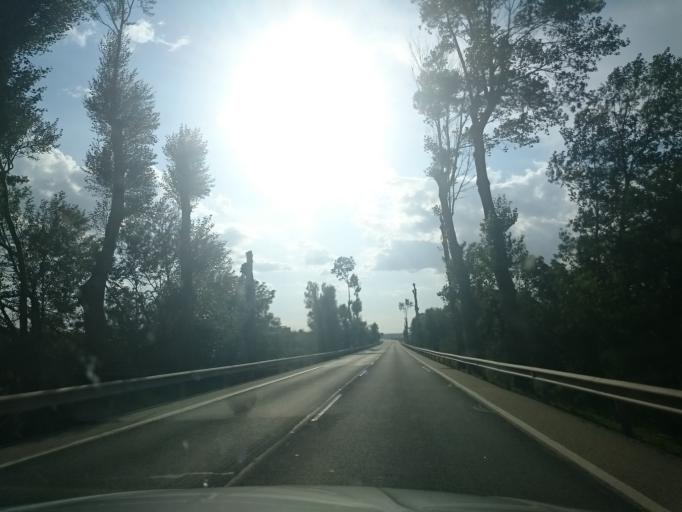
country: ES
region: Castille and Leon
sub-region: Provincia de Burgos
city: Arlanzon
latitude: 42.3497
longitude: -3.4559
